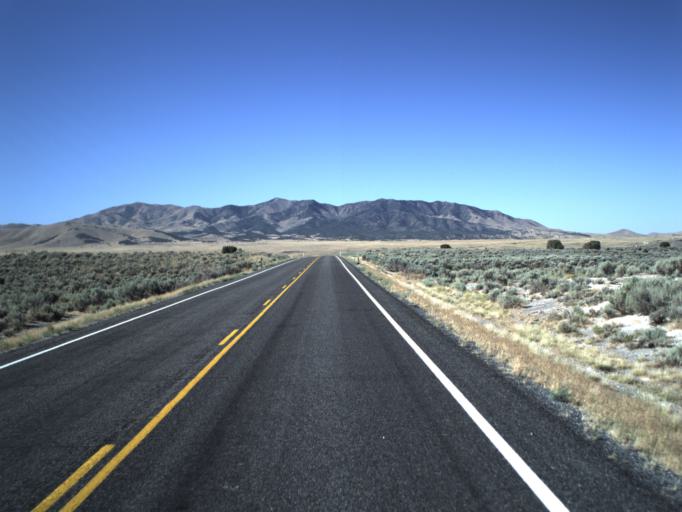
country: US
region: Utah
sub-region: Juab County
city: Mona
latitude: 39.7258
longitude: -112.1963
